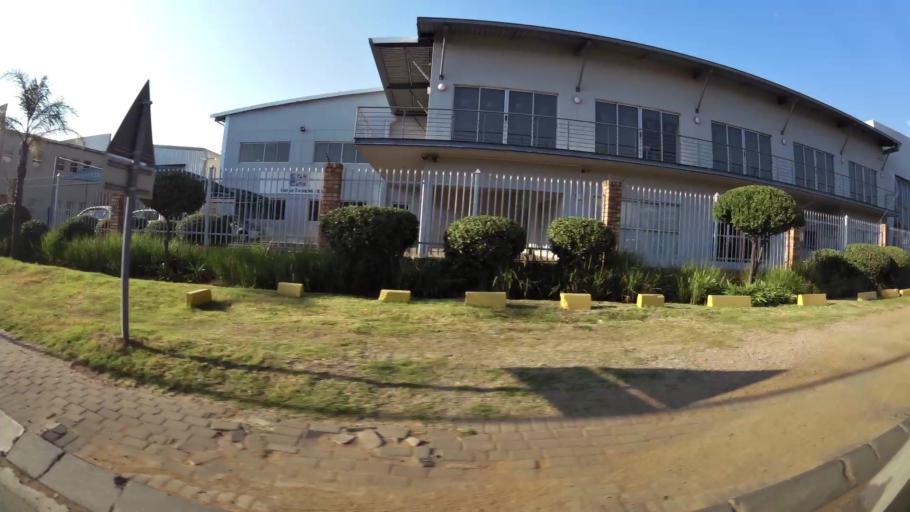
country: ZA
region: Gauteng
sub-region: City of Johannesburg Metropolitan Municipality
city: Modderfontein
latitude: -26.1513
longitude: 28.1758
